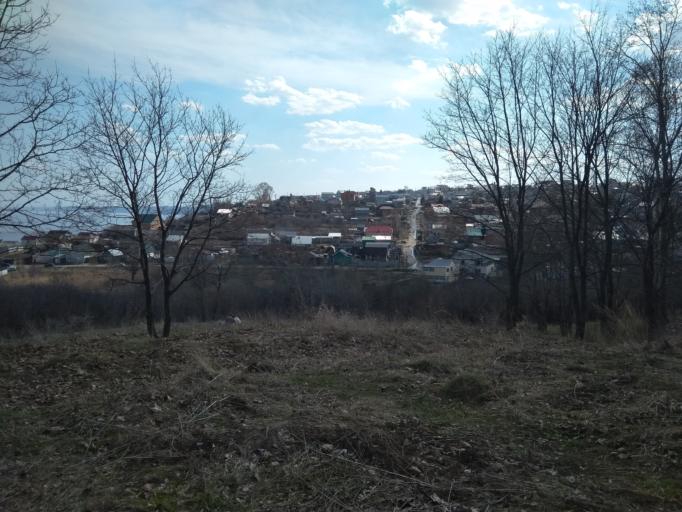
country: RU
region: Ulyanovsk
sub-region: Ulyanovskiy Rayon
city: Ulyanovsk
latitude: 54.2710
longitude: 48.3559
